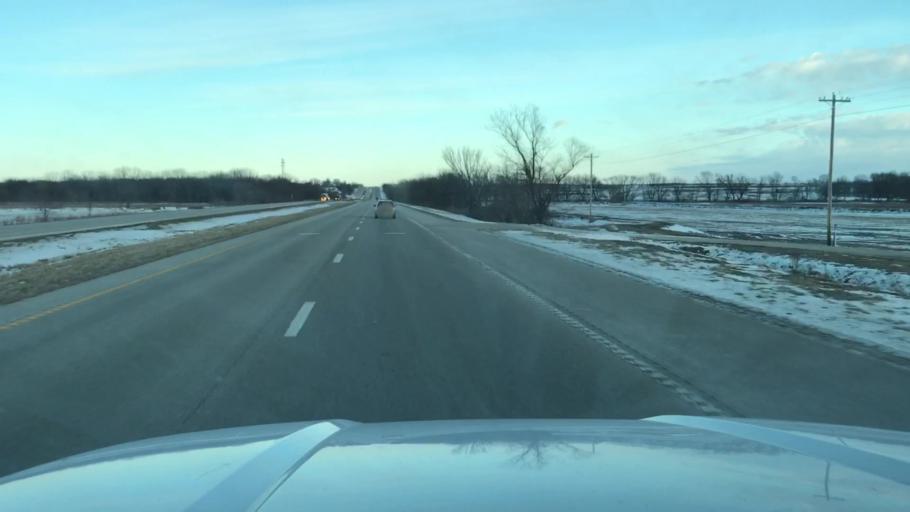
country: US
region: Missouri
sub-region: Clinton County
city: Gower
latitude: 39.7474
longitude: -94.6692
